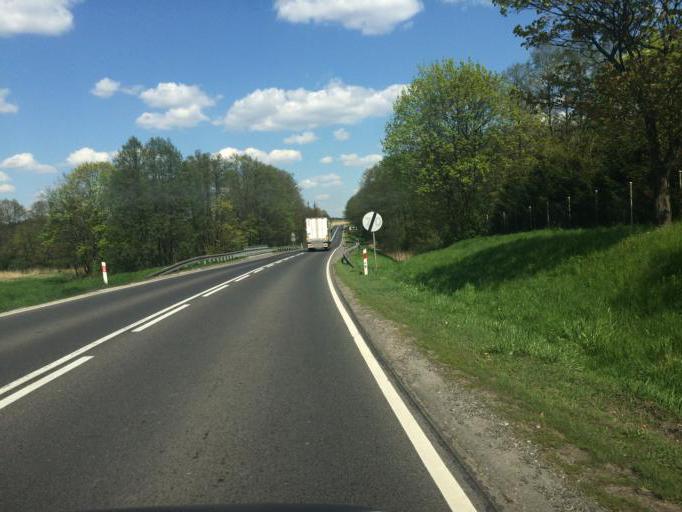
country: PL
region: Warmian-Masurian Voivodeship
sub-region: Powiat olsztynski
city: Gietrzwald
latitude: 53.7356
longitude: 20.2056
